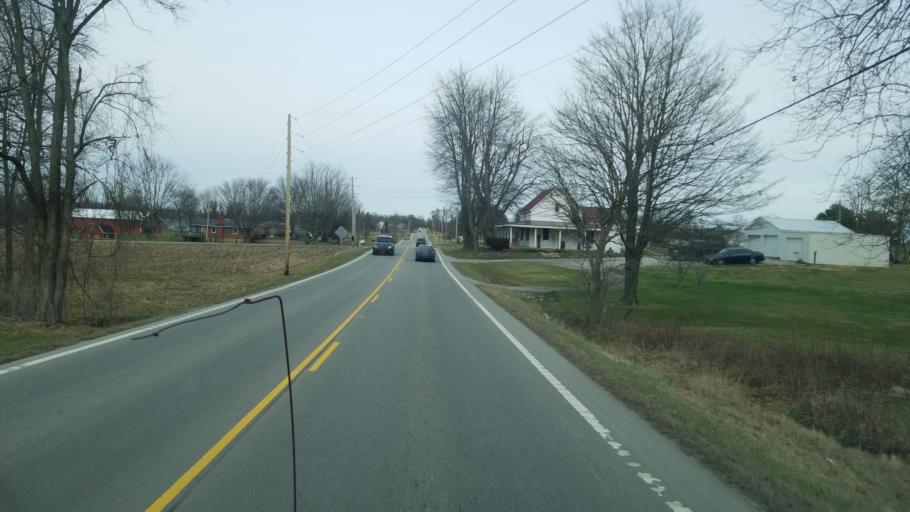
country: US
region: Ohio
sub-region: Highland County
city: Hillsboro
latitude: 39.1400
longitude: -83.6672
